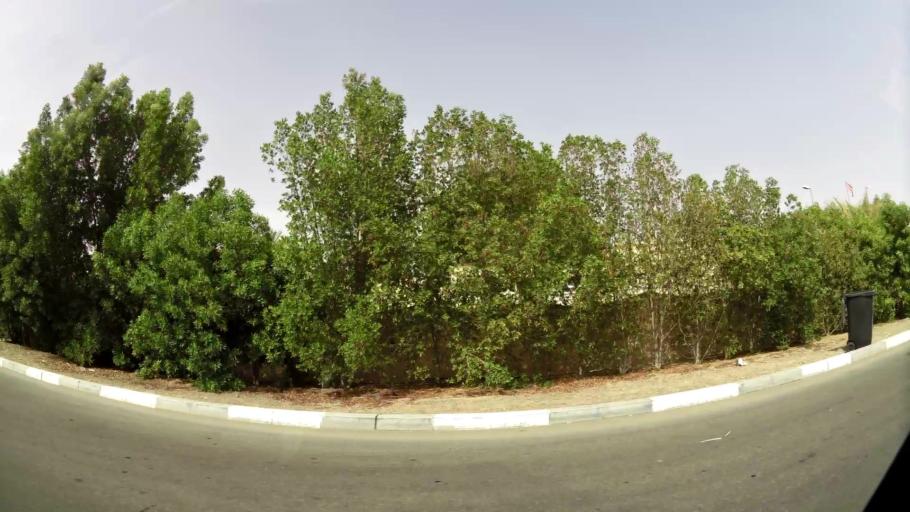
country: AE
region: Abu Dhabi
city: Al Ain
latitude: 24.1842
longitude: 55.6242
